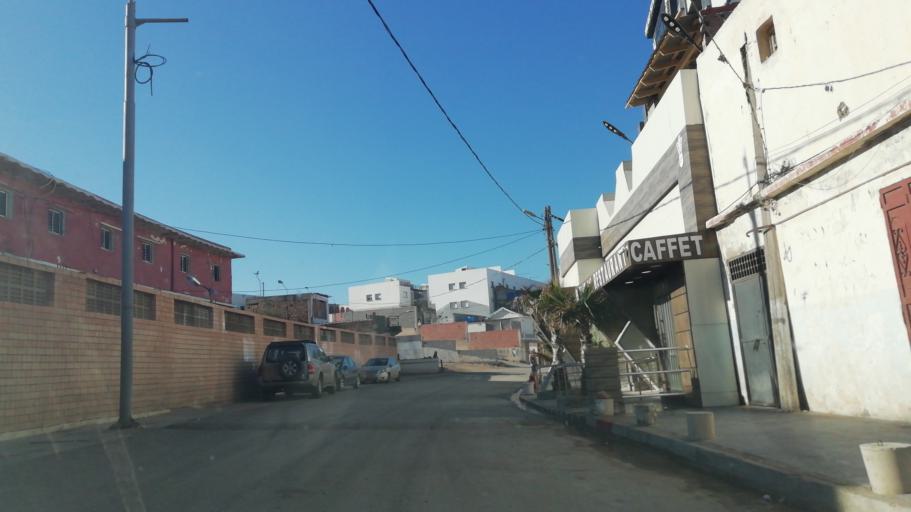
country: DZ
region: Oran
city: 'Ain el Turk
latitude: 35.7235
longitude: -0.8495
